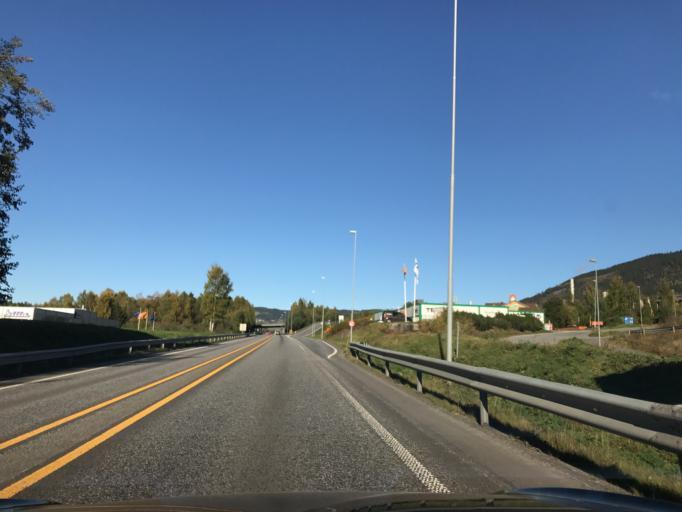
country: NO
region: Oppland
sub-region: Lillehammer
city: Lillehammer
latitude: 61.1280
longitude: 10.4361
